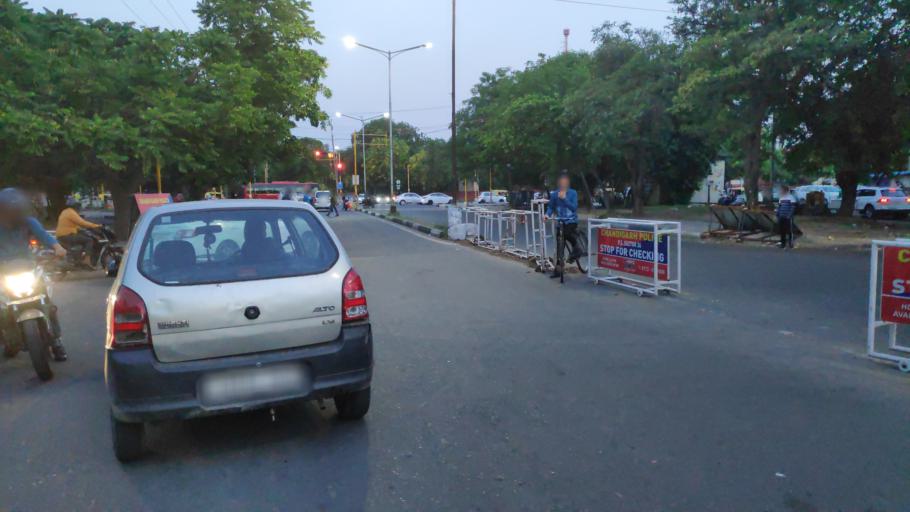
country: IN
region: Chandigarh
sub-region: Chandigarh
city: Chandigarh
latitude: 30.7234
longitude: 76.7624
